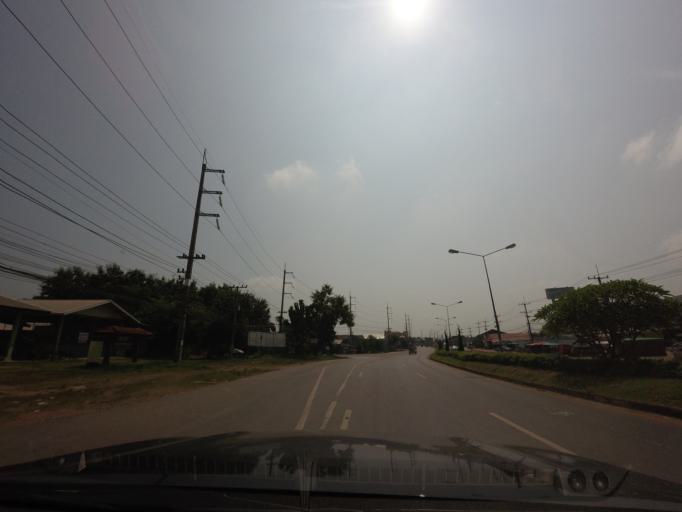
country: TH
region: Nan
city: Nan
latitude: 18.7859
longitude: 100.7440
